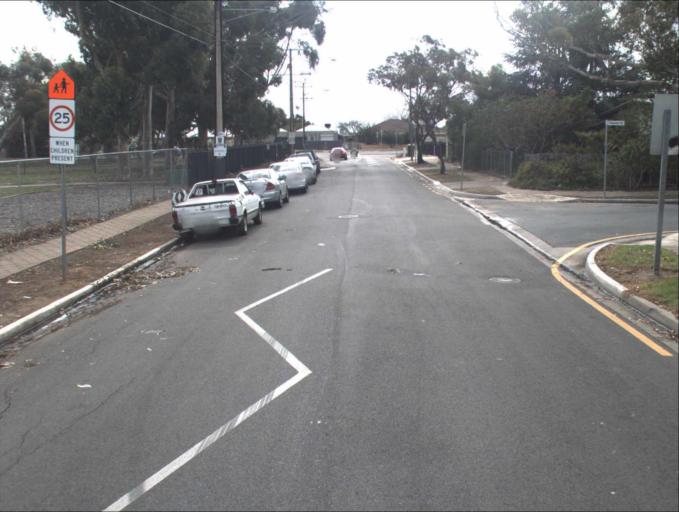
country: AU
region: South Australia
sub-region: Port Adelaide Enfield
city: Gilles Plains
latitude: -34.8468
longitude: 138.6566
